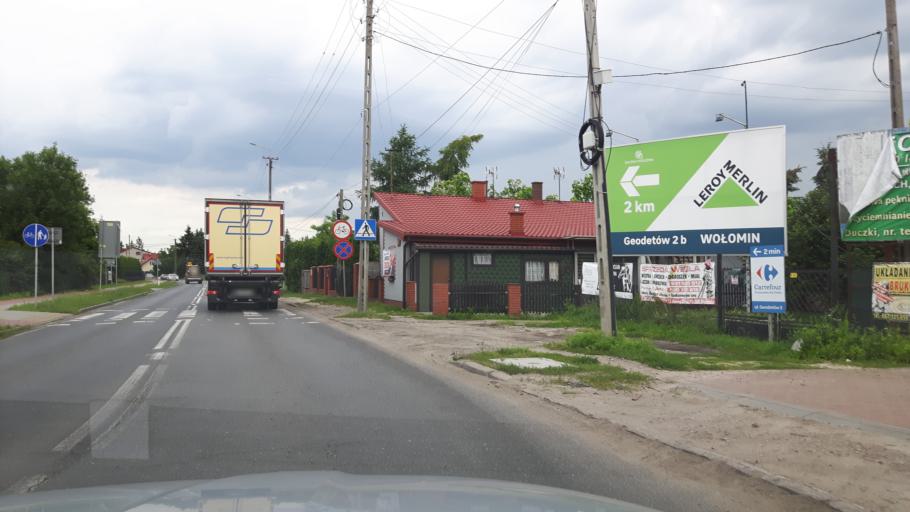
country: PL
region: Masovian Voivodeship
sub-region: Powiat wolominski
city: Nowe Lipiny
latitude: 52.3450
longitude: 21.2663
